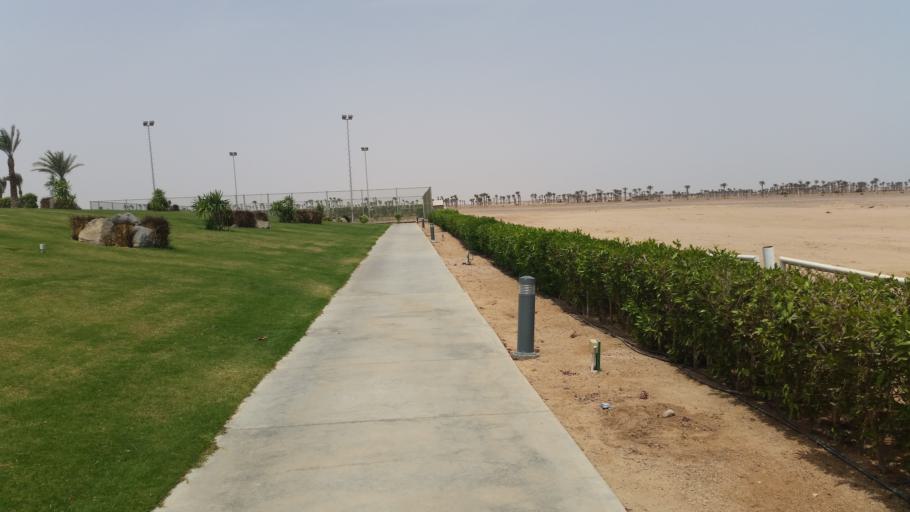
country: EG
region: Red Sea
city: Makadi Bay
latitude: 26.9840
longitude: 33.8749
